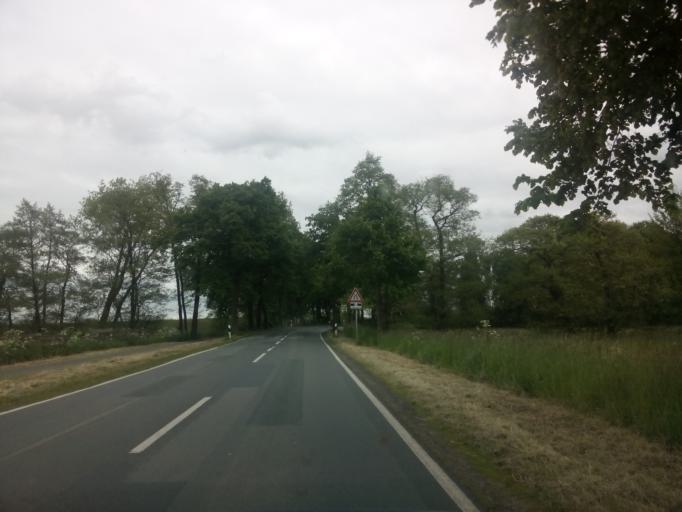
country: DE
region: Lower Saxony
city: Delmenhorst
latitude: 53.0955
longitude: 8.6540
